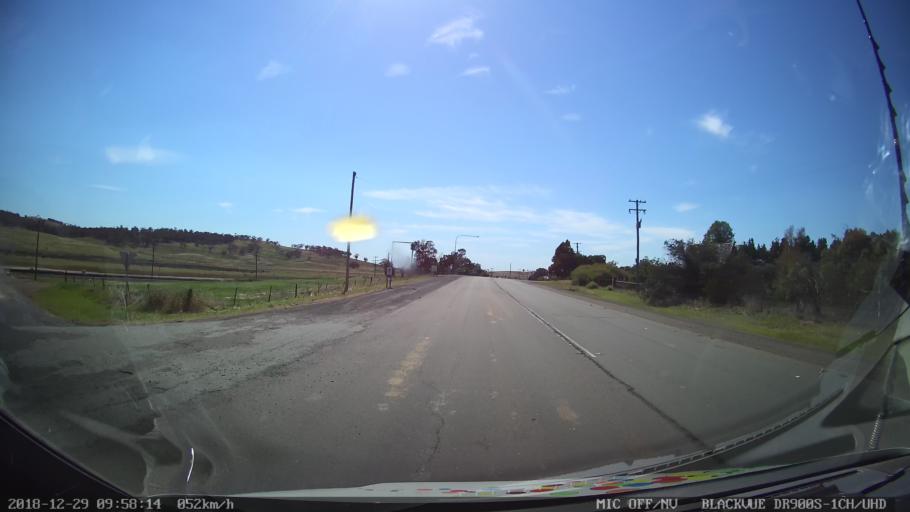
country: AU
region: New South Wales
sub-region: Goulburn Mulwaree
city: Goulburn
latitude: -34.7886
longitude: 149.4870
